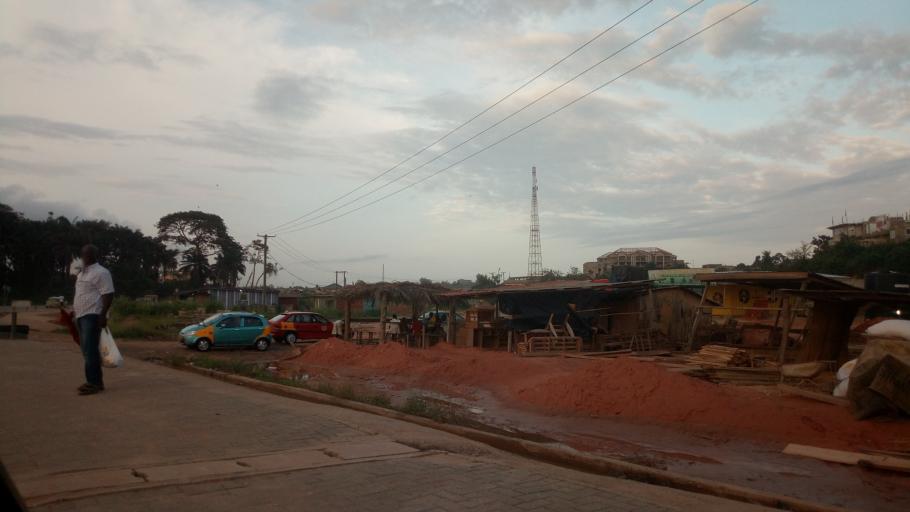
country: GH
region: Western
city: Sekondi-Takoradi
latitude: 4.9512
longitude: -1.7608
